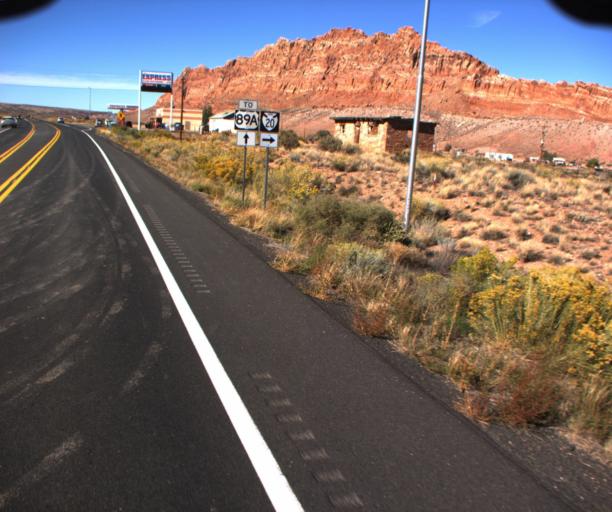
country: US
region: Arizona
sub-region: Coconino County
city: Tuba City
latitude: 36.3024
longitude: -111.4590
